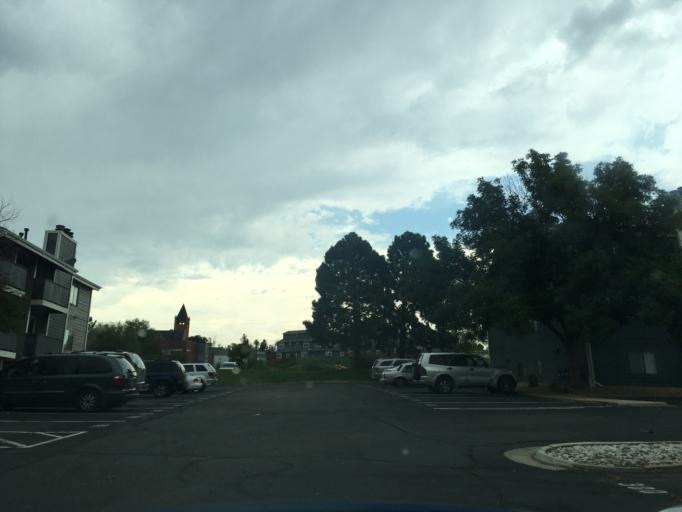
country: US
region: Colorado
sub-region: Arapahoe County
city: Sheridan
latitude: 39.6576
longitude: -105.0266
